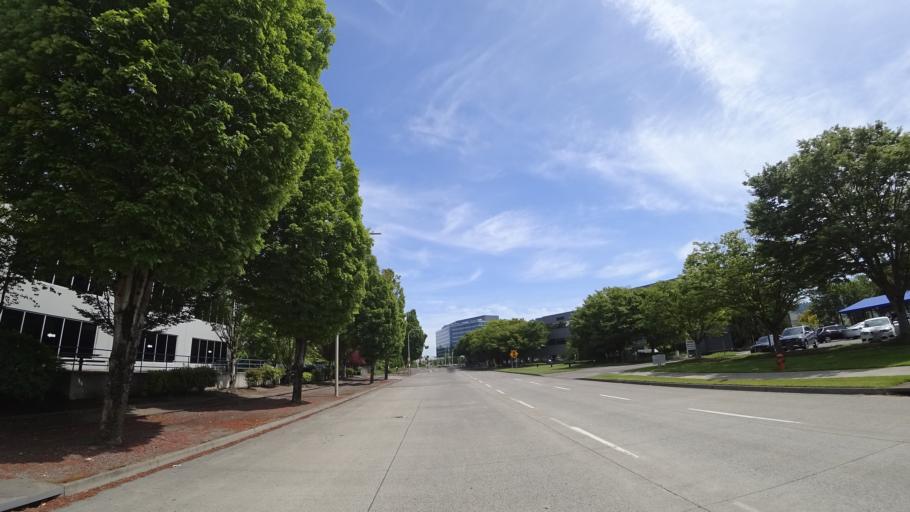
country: US
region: Oregon
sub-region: Multnomah County
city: Portland
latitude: 45.5577
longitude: -122.7069
